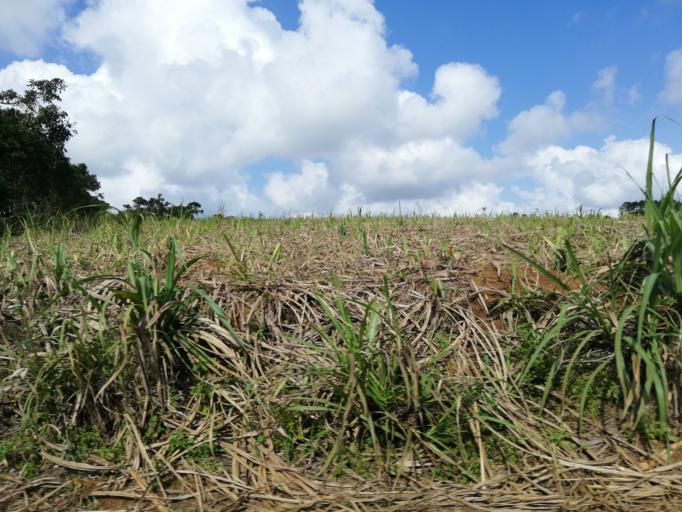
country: MU
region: Pamplemousses
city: Creve Coeur
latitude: -20.2046
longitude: 57.5593
